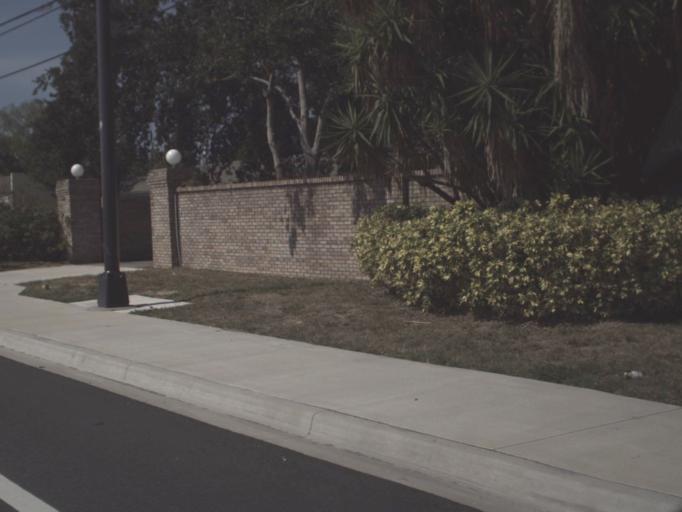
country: US
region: Florida
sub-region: Brevard County
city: Cocoa
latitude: 28.3739
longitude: -80.7365
